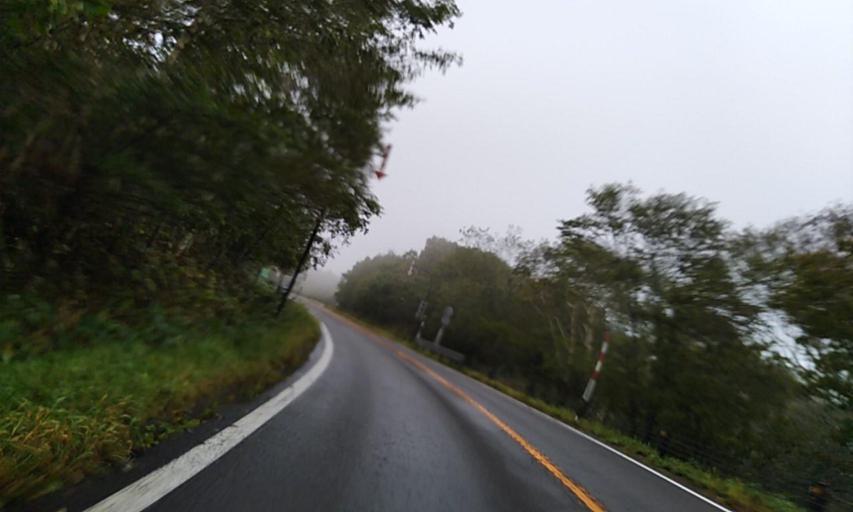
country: JP
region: Hokkaido
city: Bihoro
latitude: 43.5428
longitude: 144.5084
